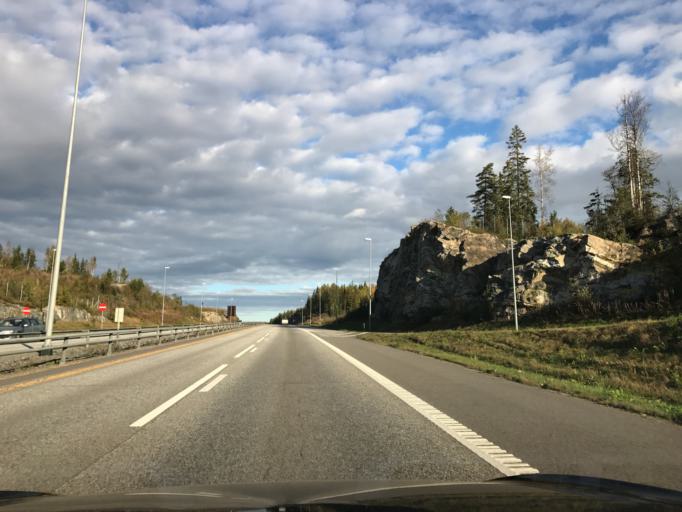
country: NO
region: Akershus
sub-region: Eidsvoll
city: Raholt
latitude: 60.2549
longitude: 11.1804
